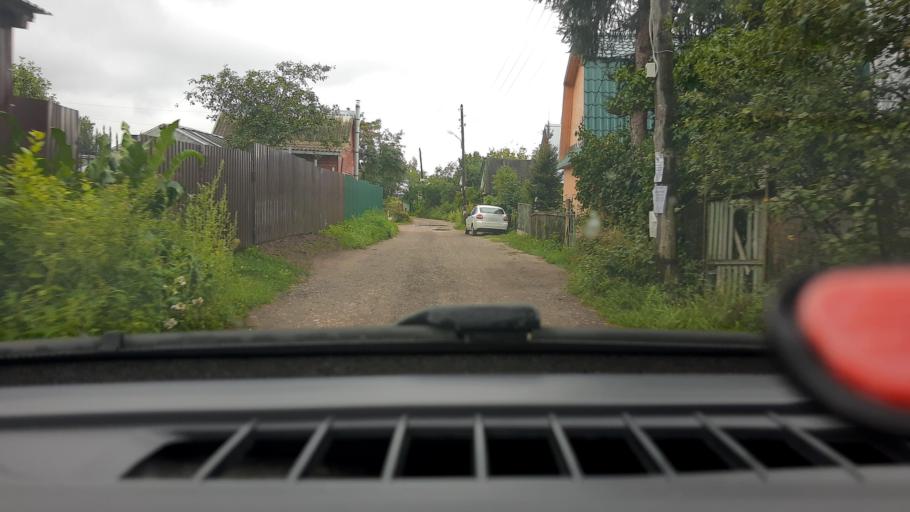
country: RU
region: Nizjnij Novgorod
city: Gorbatovka
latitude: 56.3178
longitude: 43.8365
